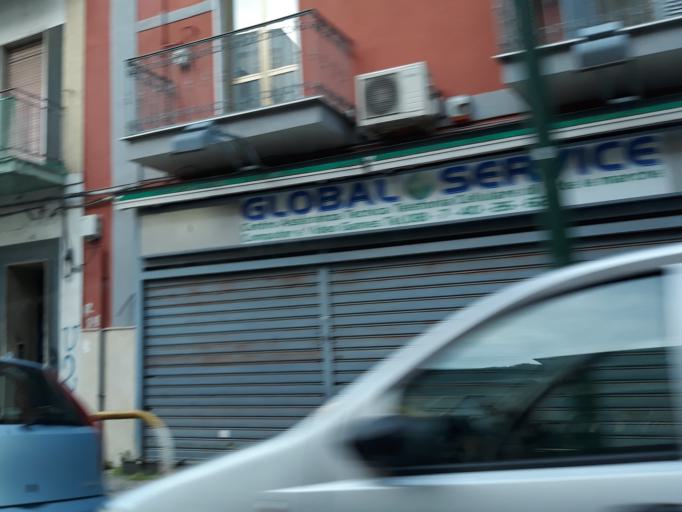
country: IT
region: Campania
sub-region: Provincia di Napoli
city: Mugnano di Napoli
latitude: 40.8850
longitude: 14.2293
